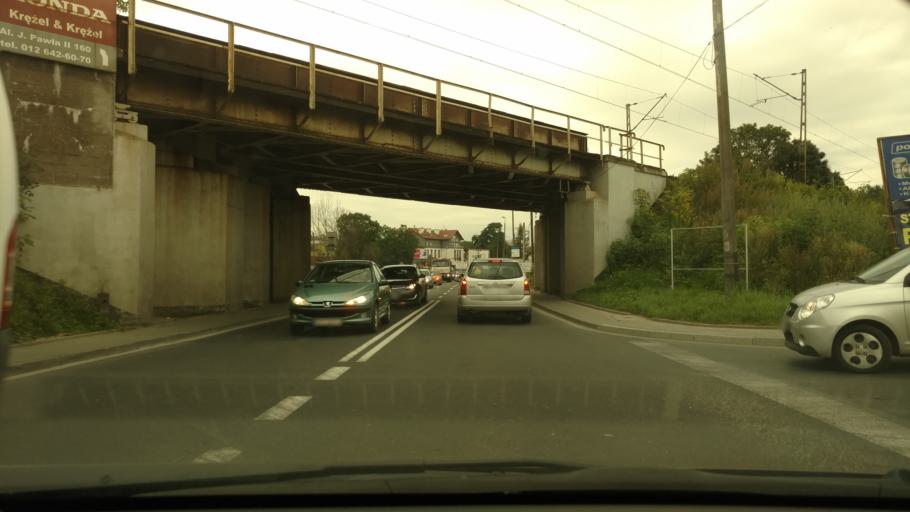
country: PL
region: Lesser Poland Voivodeship
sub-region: Krakow
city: Krakow
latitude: 50.0939
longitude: 19.9610
